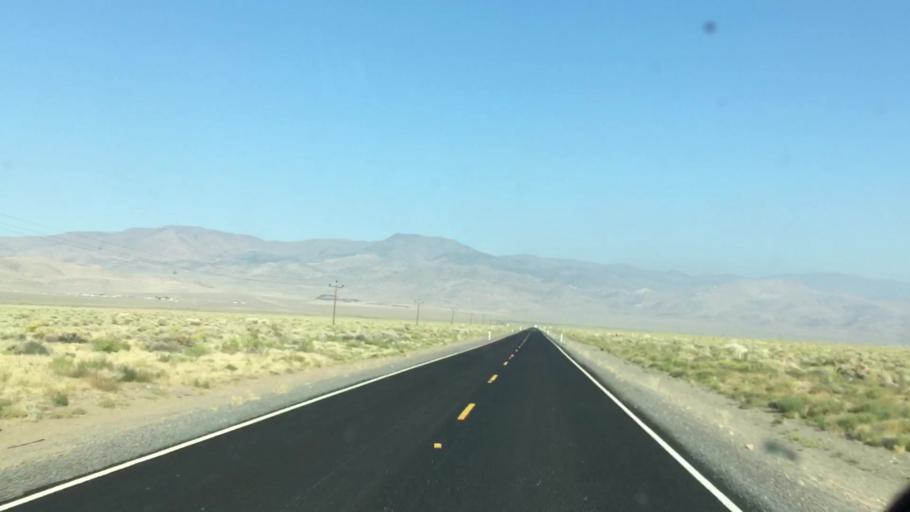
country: US
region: Nevada
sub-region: Lyon County
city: Fernley
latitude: 39.6450
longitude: -119.3095
